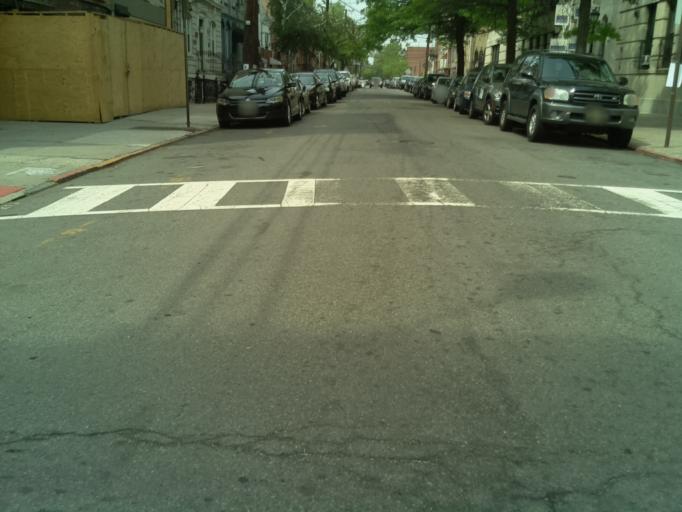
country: US
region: New Jersey
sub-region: Hudson County
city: Hoboken
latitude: 40.7403
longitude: -74.0319
